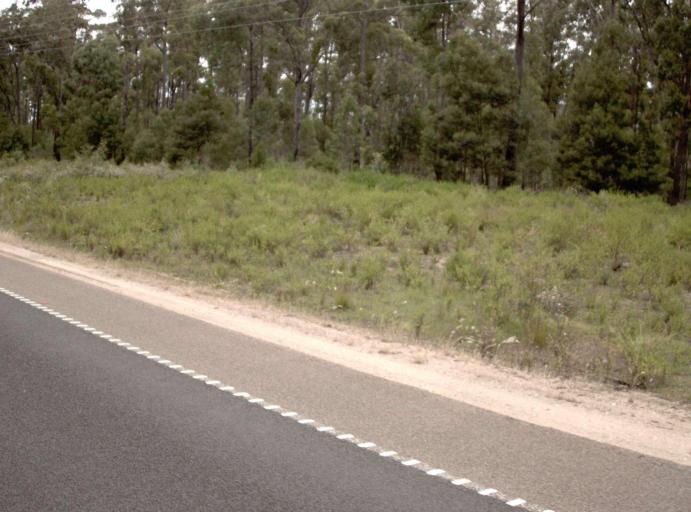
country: AU
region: Victoria
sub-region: East Gippsland
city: Lakes Entrance
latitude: -37.7164
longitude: 148.0764
